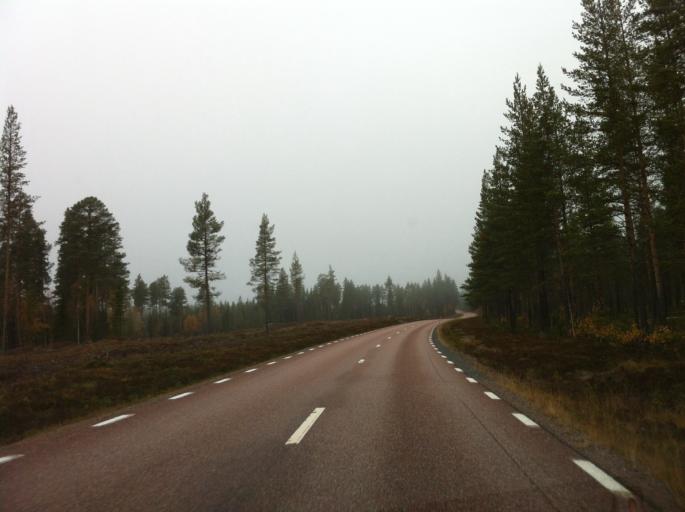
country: NO
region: Hedmark
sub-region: Trysil
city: Innbygda
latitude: 61.7772
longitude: 12.9439
